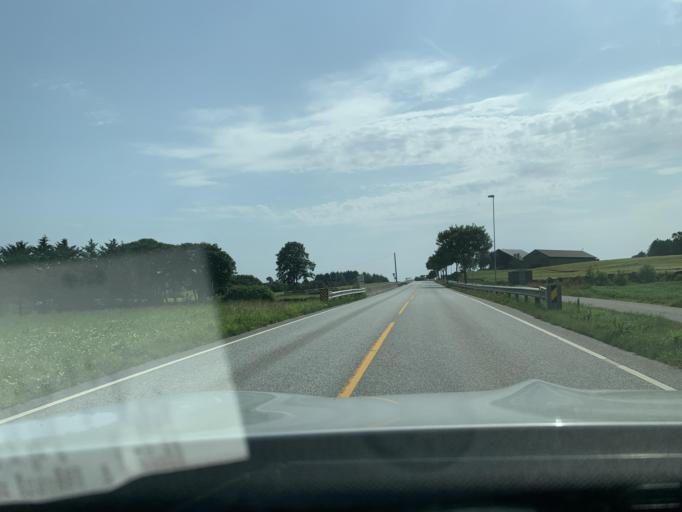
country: NO
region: Rogaland
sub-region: Klepp
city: Kleppe
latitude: 58.7653
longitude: 5.6268
